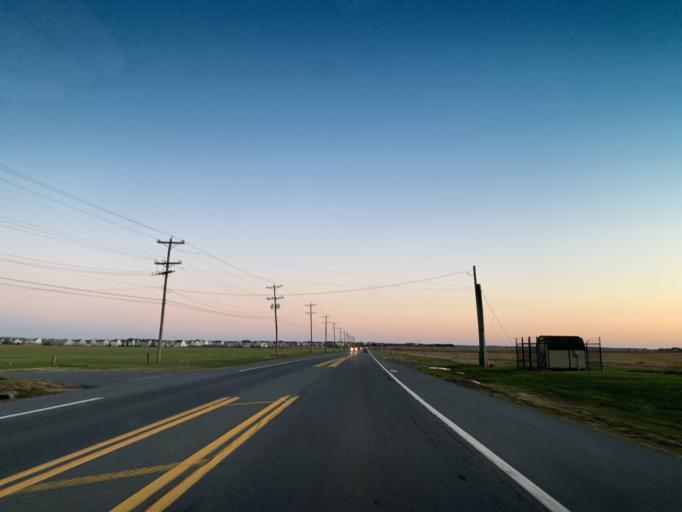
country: US
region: Delaware
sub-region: New Castle County
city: Middletown
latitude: 39.4368
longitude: -75.7449
